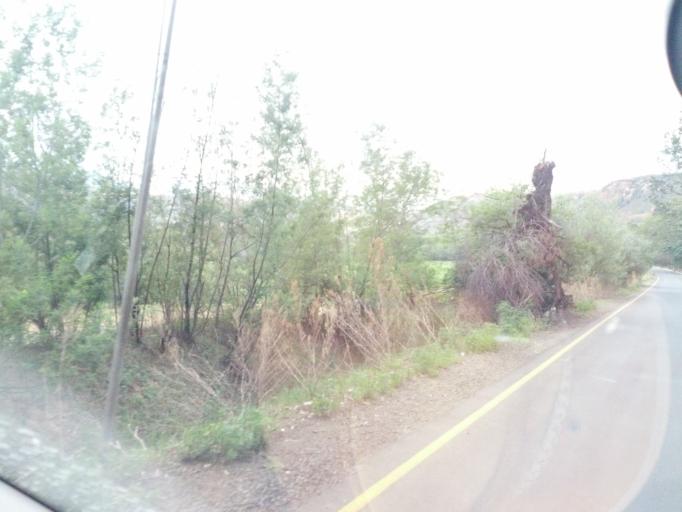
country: LS
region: Maseru
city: Nako
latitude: -29.4579
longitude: 27.7244
